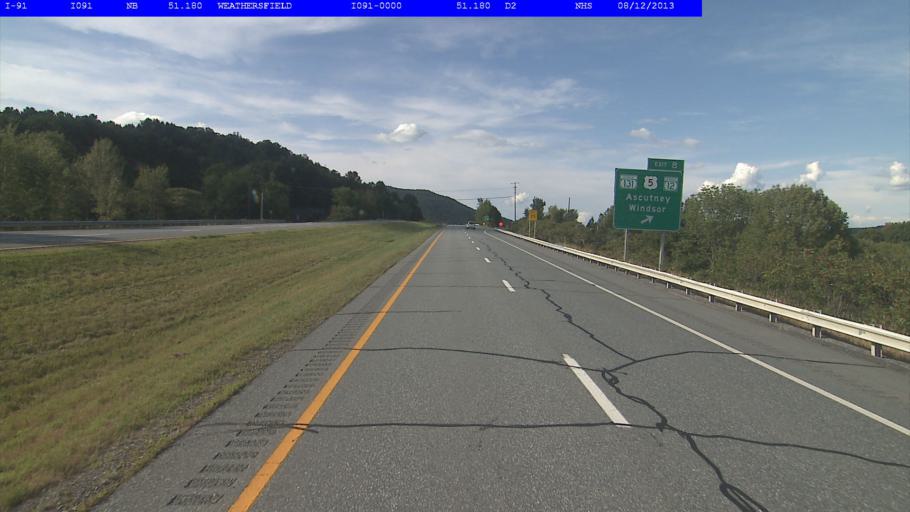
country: US
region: New Hampshire
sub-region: Sullivan County
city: Claremont
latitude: 43.3999
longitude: -72.4144
